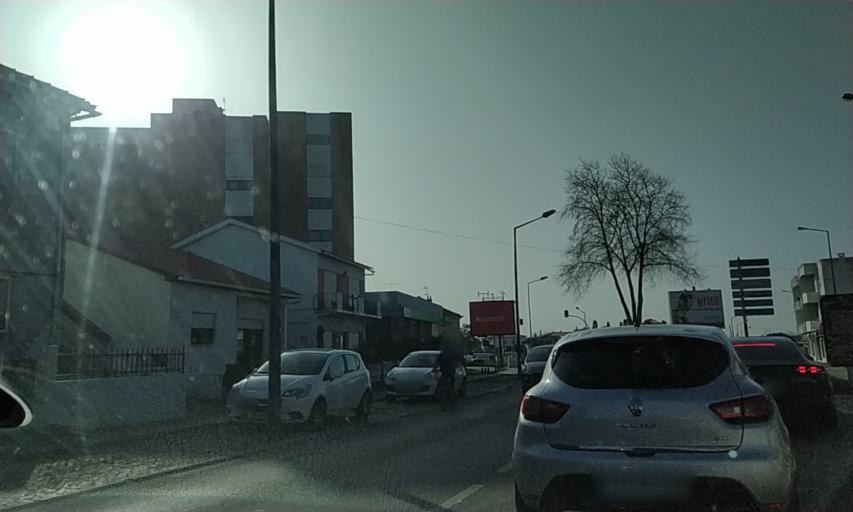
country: PT
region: Leiria
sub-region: Marinha Grande
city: Marinha Grande
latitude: 39.7495
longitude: -8.9208
